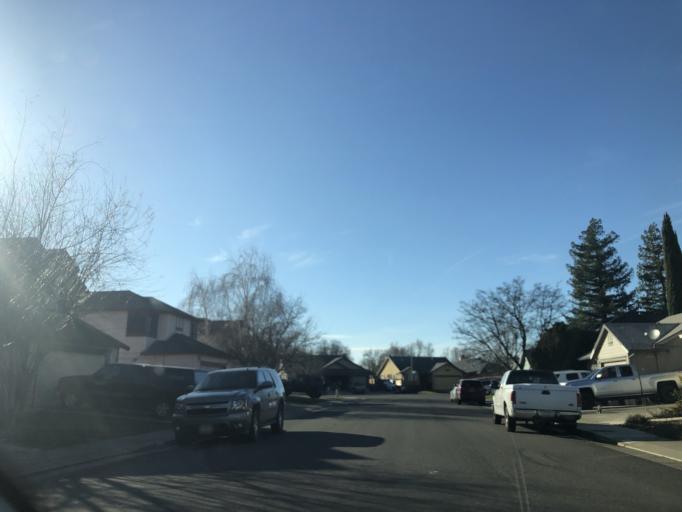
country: US
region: California
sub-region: Yolo County
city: Woodland
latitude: 38.6648
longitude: -121.7489
